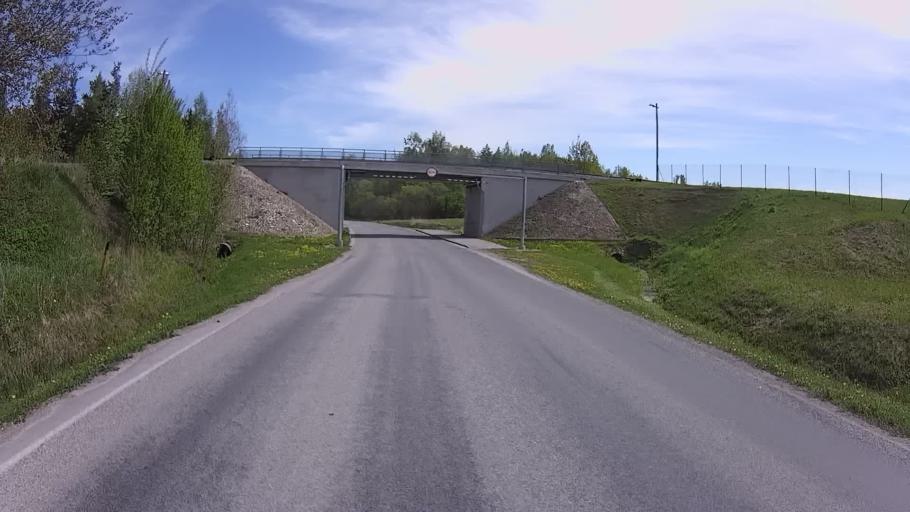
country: EE
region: Valgamaa
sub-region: Valga linn
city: Valga
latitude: 57.7779
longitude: 26.0675
